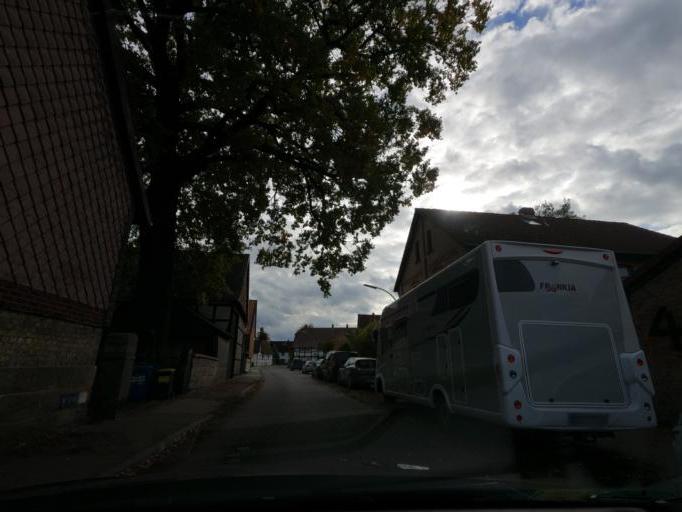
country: DE
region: Lower Saxony
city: Leiferde
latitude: 52.2097
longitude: 10.5218
